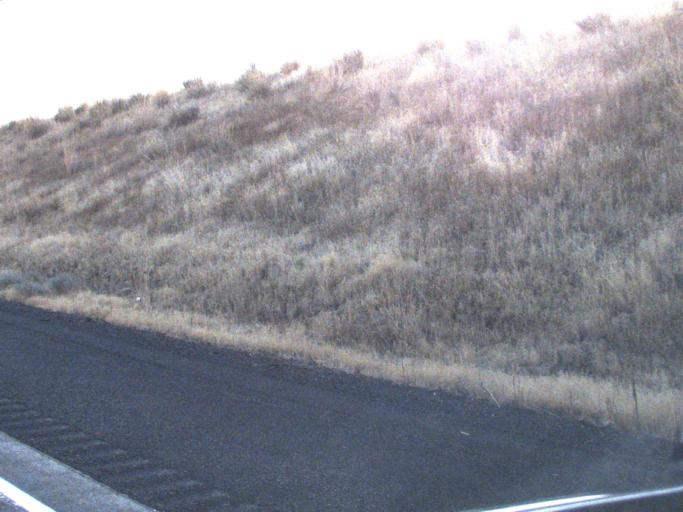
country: US
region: Washington
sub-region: Franklin County
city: Connell
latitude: 46.8186
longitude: -118.6913
